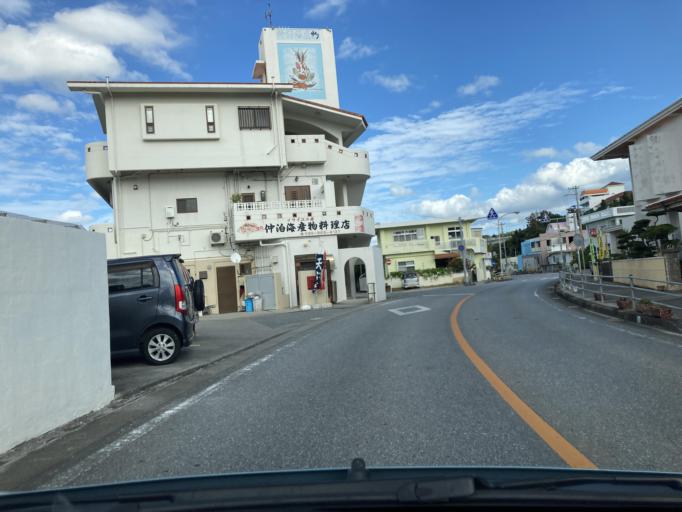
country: JP
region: Okinawa
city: Ishikawa
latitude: 26.4373
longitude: 127.7996
